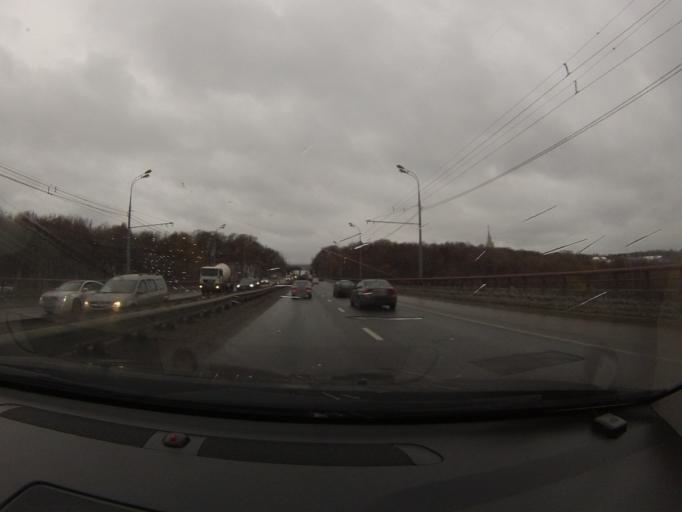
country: RU
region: Moscow
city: Luzhniki
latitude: 55.7091
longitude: 37.5575
